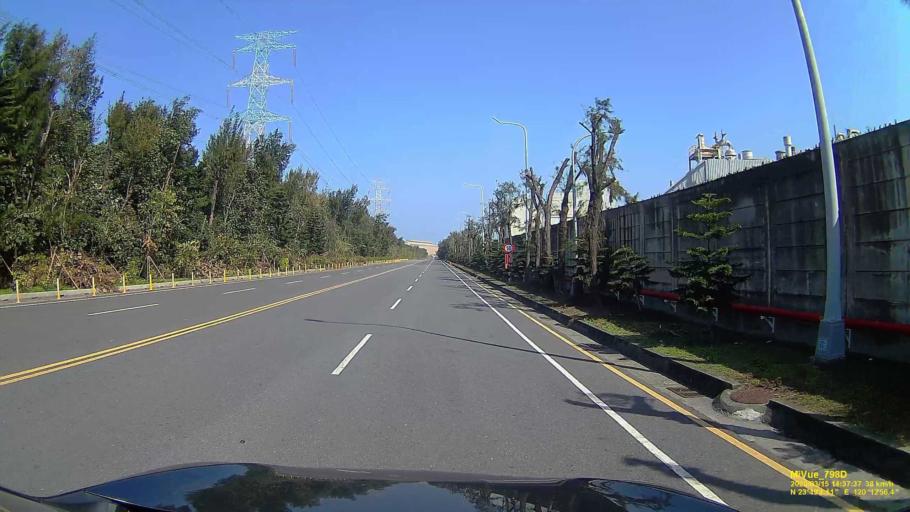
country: TW
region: Taiwan
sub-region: Yunlin
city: Douliu
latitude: 23.8178
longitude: 120.2159
